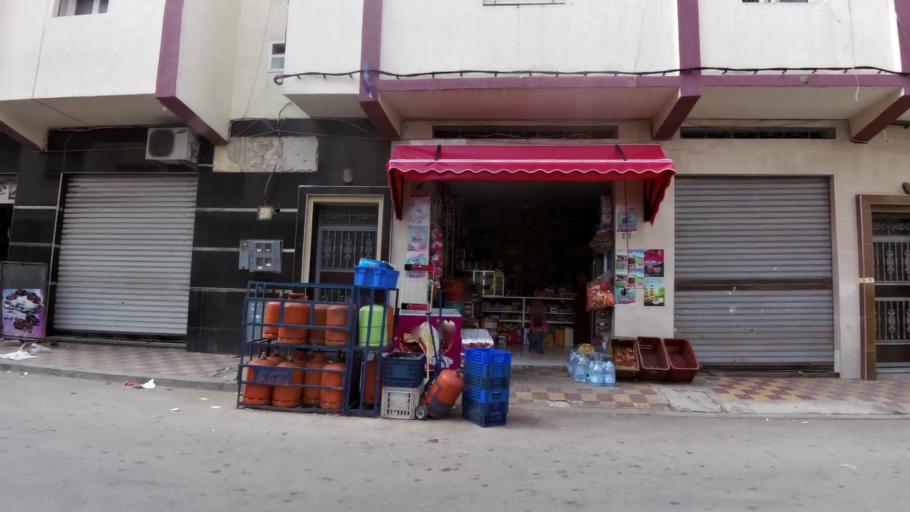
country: MA
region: Tanger-Tetouan
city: Tetouan
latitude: 35.5861
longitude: -5.3499
